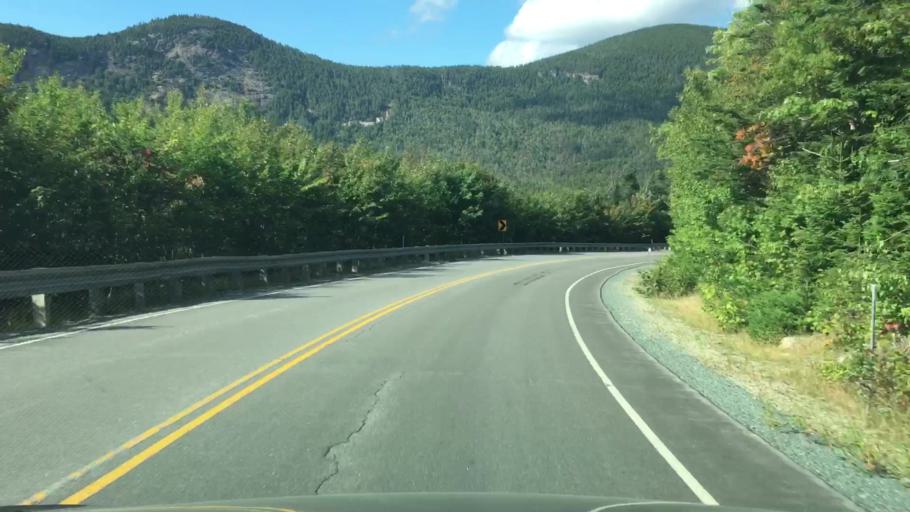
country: US
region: New Hampshire
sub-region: Grafton County
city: Woodstock
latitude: 44.0315
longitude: -71.4991
